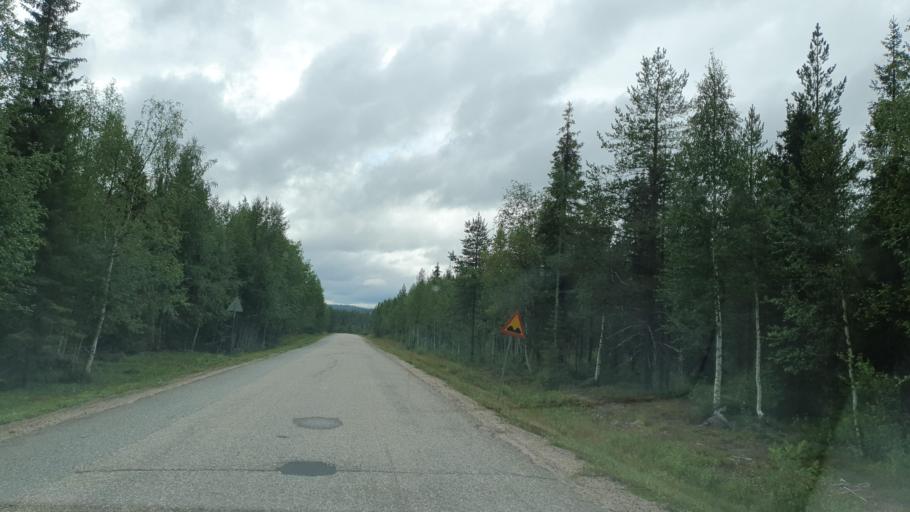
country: FI
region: Lapland
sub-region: Tunturi-Lappi
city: Kolari
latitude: 67.5088
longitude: 24.2432
